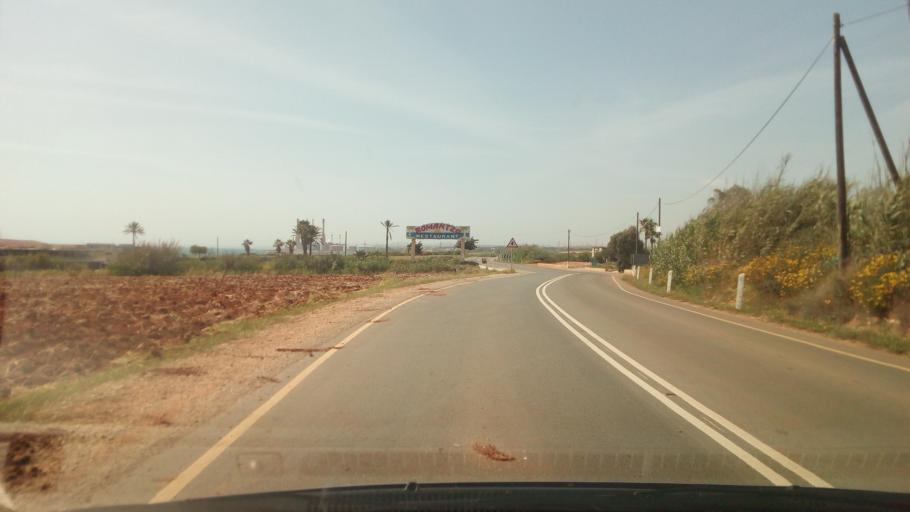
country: CY
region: Larnaka
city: Xylotymbou
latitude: 34.9806
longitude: 33.7707
